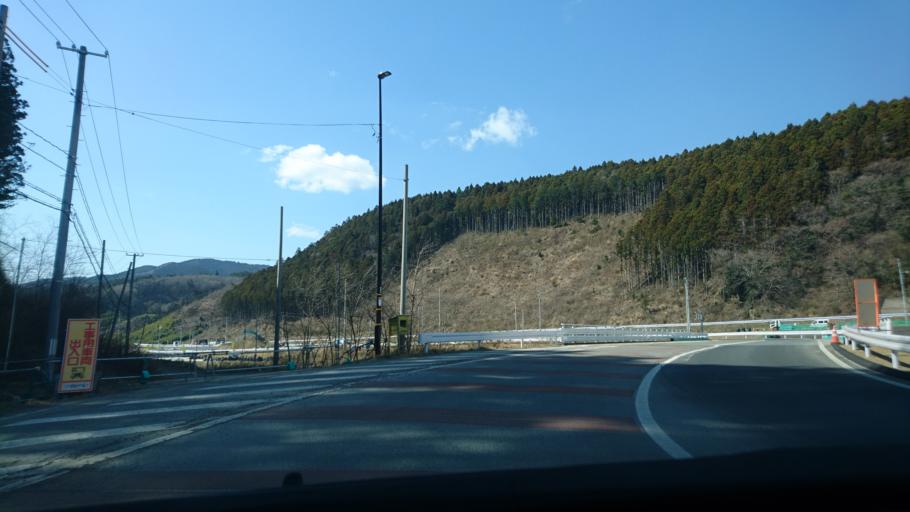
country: JP
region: Miyagi
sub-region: Oshika Gun
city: Onagawa Cho
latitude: 38.6465
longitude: 141.4368
